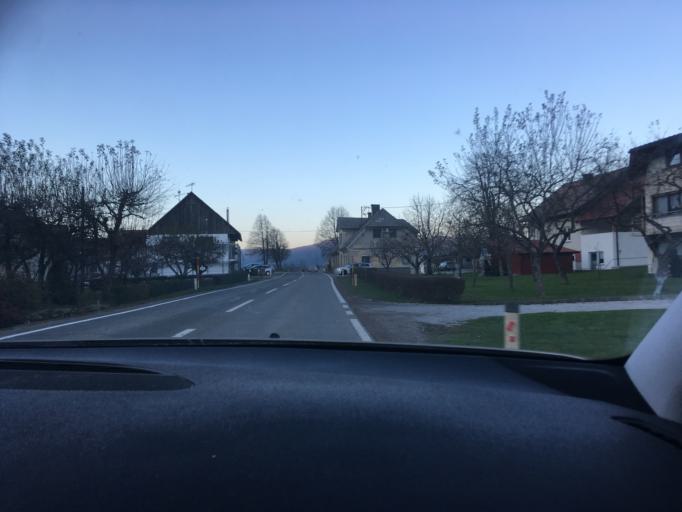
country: SI
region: Kocevje
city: Kocevje
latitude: 45.6601
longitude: 14.8406
